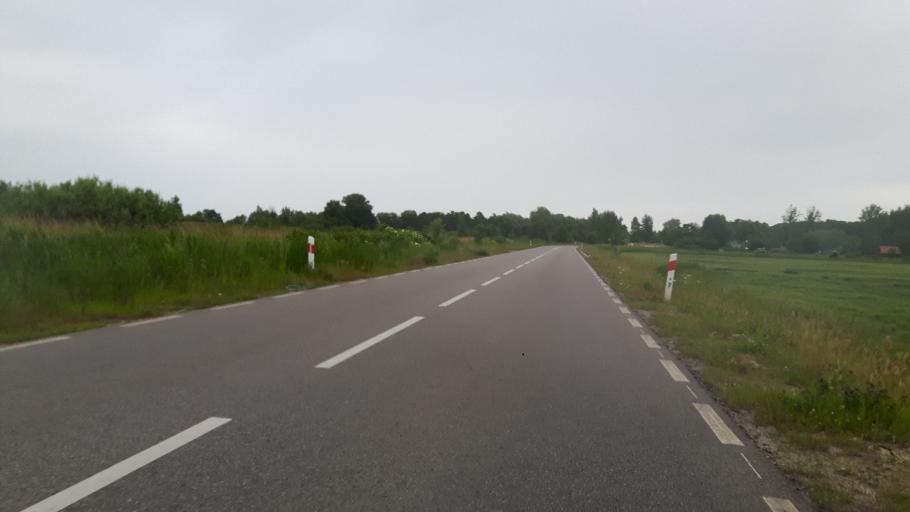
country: PL
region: Warmian-Masurian Voivodeship
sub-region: Powiat elblaski
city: Elblag
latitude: 54.2307
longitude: 19.3904
